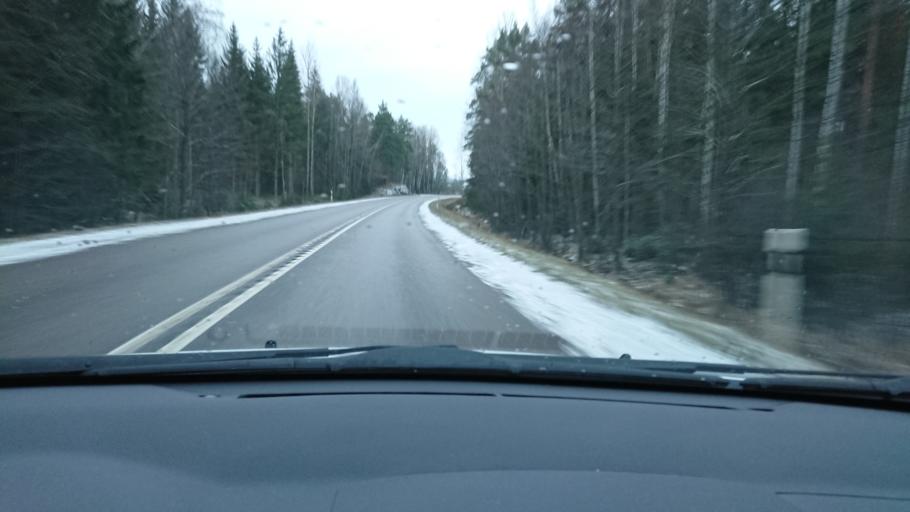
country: SE
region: Kalmar
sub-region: Hultsfreds Kommun
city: Hultsfred
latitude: 57.4945
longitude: 15.8216
